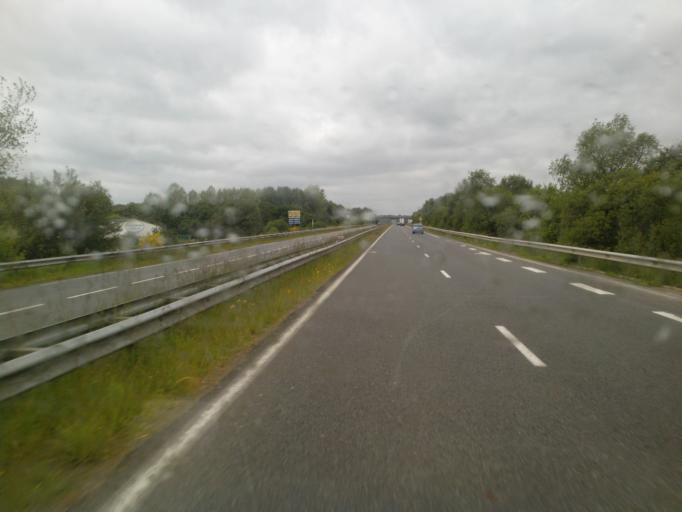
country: FR
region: Brittany
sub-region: Departement des Cotes-d'Armor
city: Belle-Isle-en-Terre
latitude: 48.5523
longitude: -3.3776
